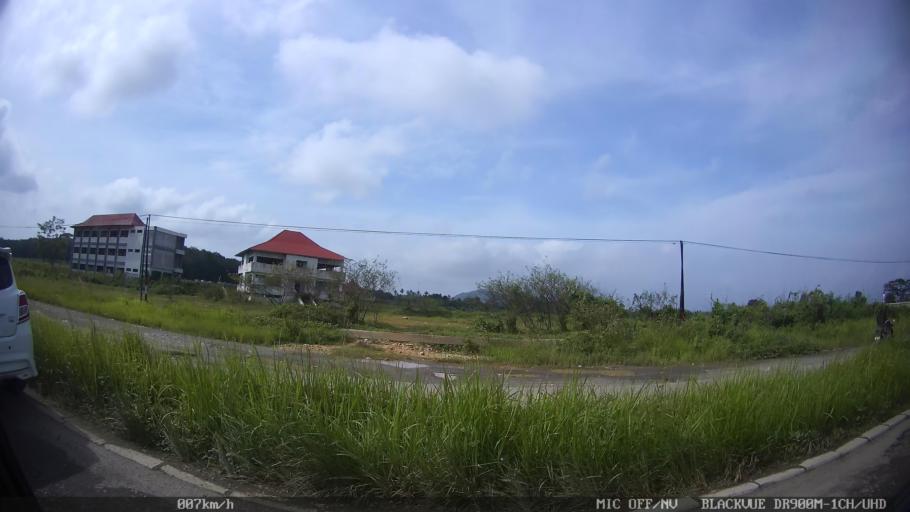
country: ID
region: Lampung
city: Kedaton
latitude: -5.3736
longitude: 105.3180
